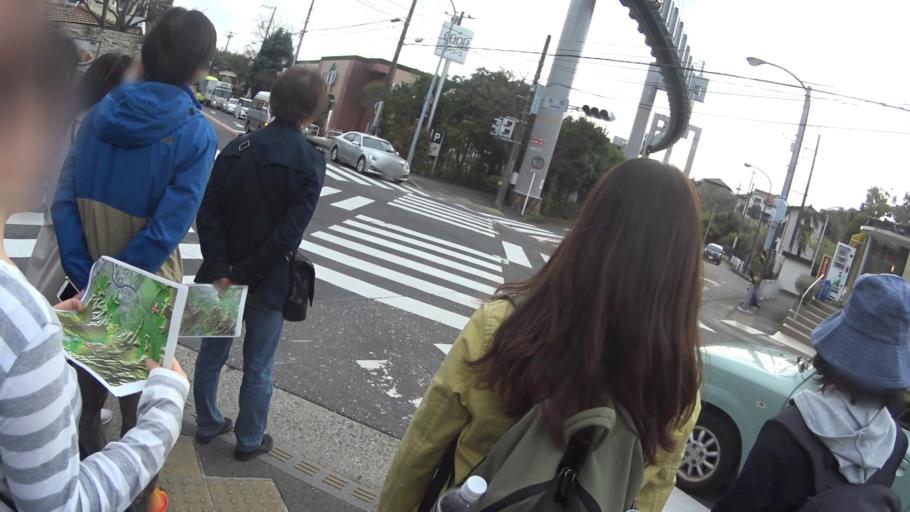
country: JP
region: Kanagawa
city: Fujisawa
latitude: 35.3217
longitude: 139.5071
